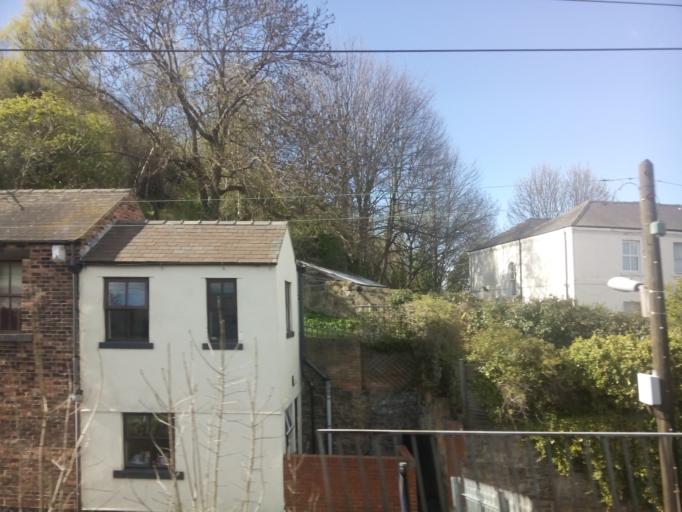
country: GB
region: England
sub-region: County Durham
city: Durham
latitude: 54.7762
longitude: -1.5884
